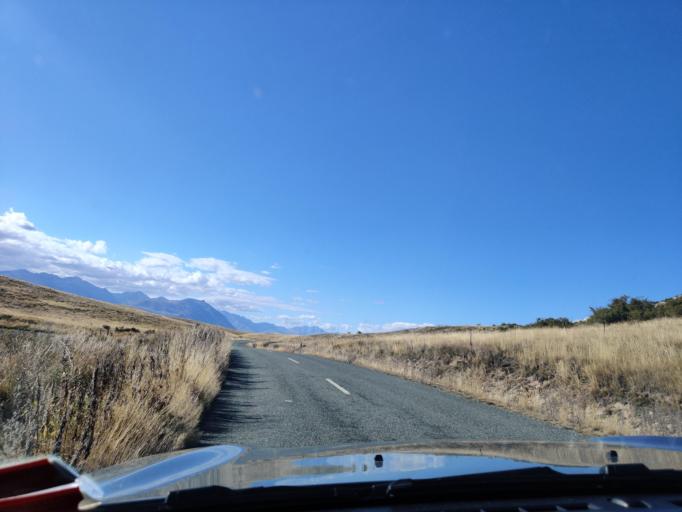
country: NZ
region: Canterbury
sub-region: Timaru District
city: Pleasant Point
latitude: -43.9777
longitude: 170.4636
